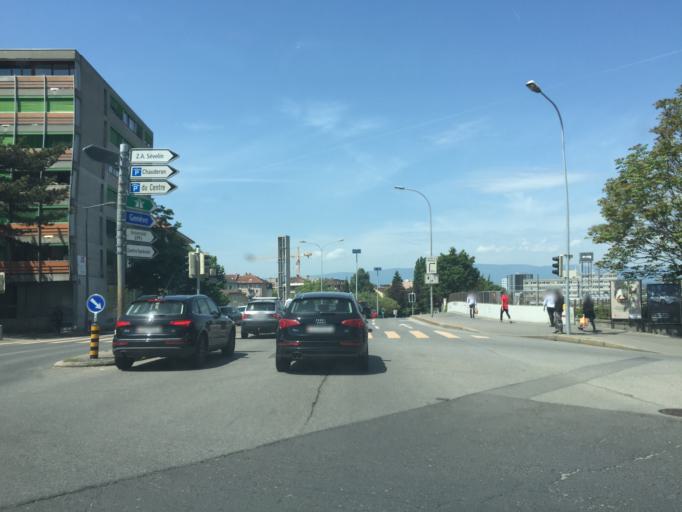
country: CH
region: Vaud
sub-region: Lausanne District
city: Lausanne
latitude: 46.5211
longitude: 6.6161
